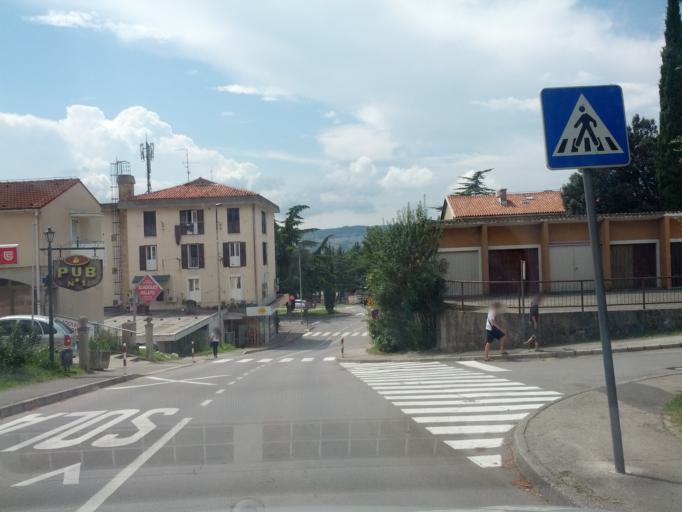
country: SI
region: Koper-Capodistria
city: Ankaran
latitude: 45.5799
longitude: 13.7371
